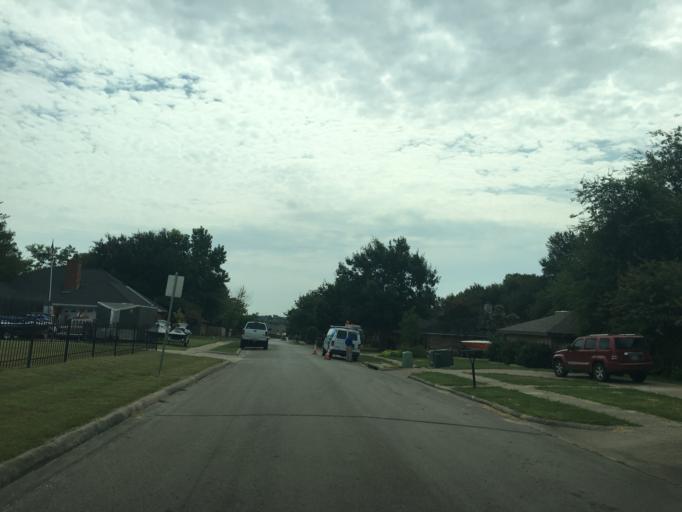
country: US
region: Texas
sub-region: Collin County
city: Wylie
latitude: 33.0139
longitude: -96.5314
